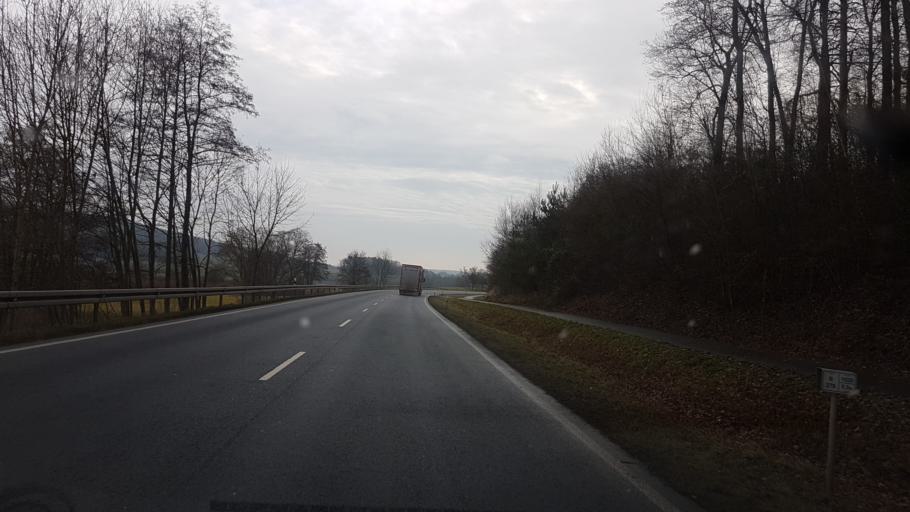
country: DE
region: Bavaria
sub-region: Regierungsbezirk Unterfranken
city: Rentweinsdorf
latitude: 50.0568
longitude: 10.8090
